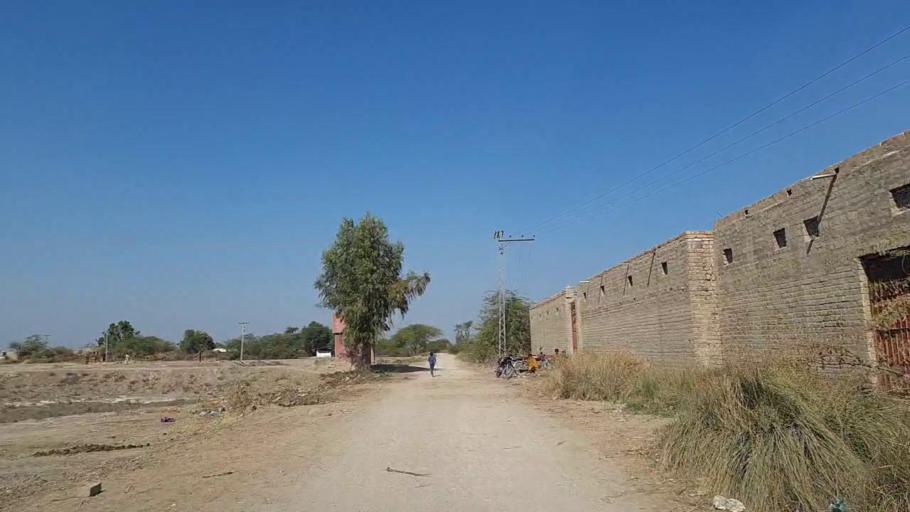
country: PK
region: Sindh
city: Nawabshah
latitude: 26.2534
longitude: 68.4411
